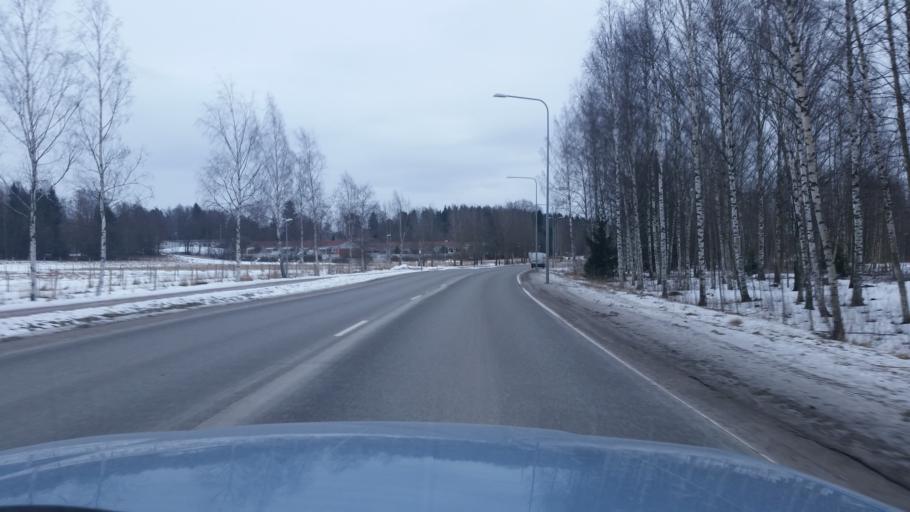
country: FI
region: Uusimaa
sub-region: Helsinki
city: Vantaa
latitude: 60.2659
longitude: 25.0385
